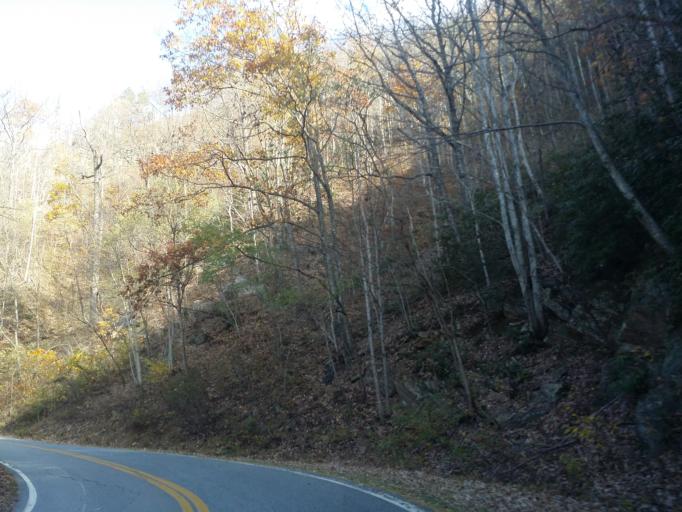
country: US
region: North Carolina
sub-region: McDowell County
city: Marion
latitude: 35.7563
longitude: -82.1536
